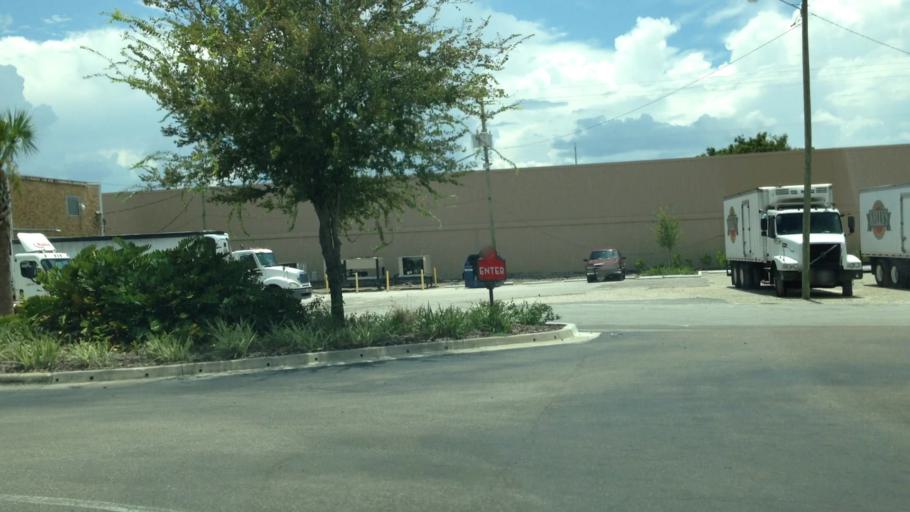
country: US
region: Florida
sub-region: Hillsborough County
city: Tampa
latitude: 27.8928
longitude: -82.5180
